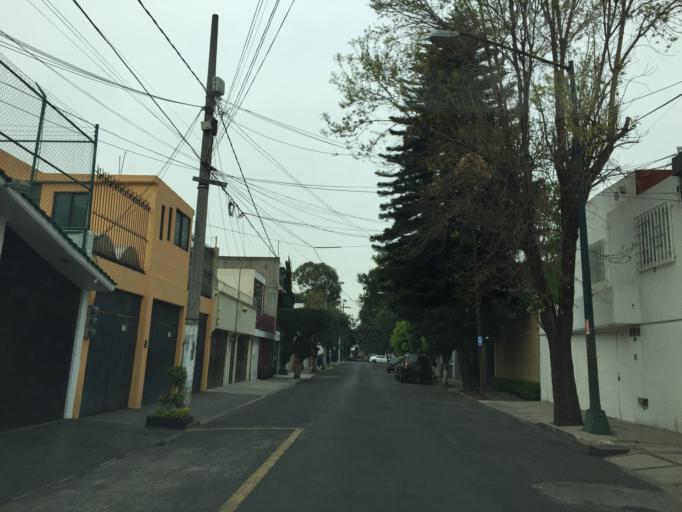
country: MX
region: Mexico
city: Colonia Lindavista
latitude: 19.4942
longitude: -99.1260
